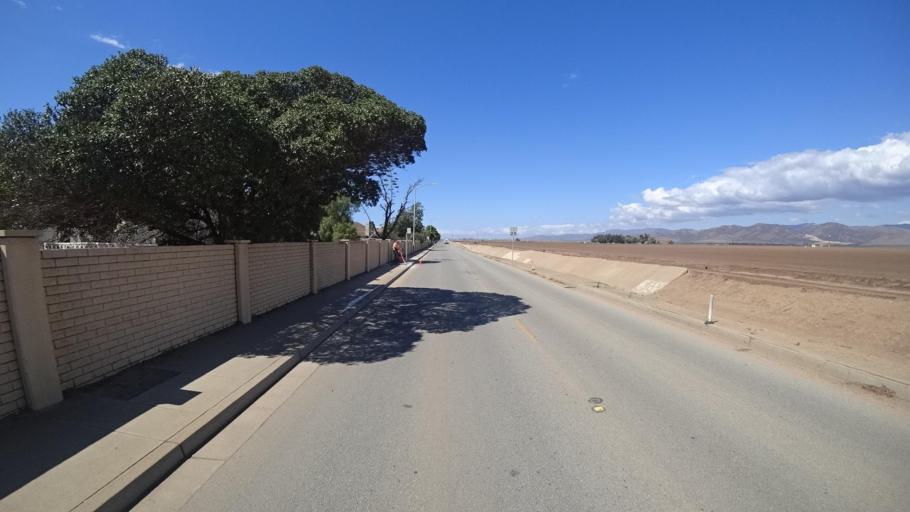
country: US
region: California
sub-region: Monterey County
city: Gonzales
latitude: 36.5204
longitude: -121.4402
